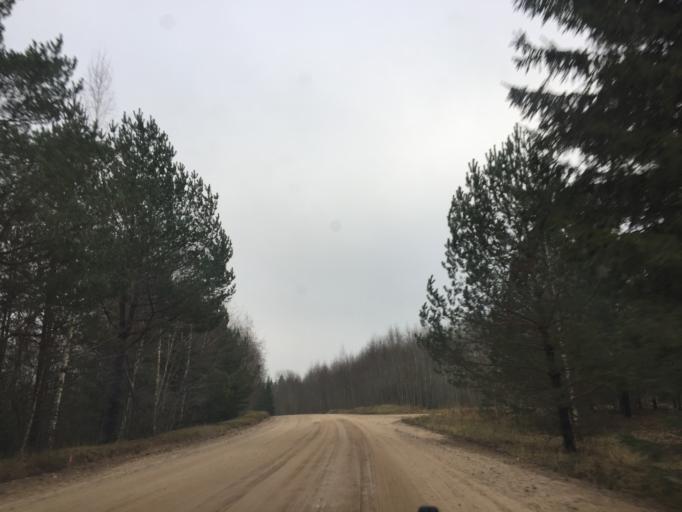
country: LV
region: Limbazu Rajons
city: Limbazi
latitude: 57.5937
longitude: 24.6232
